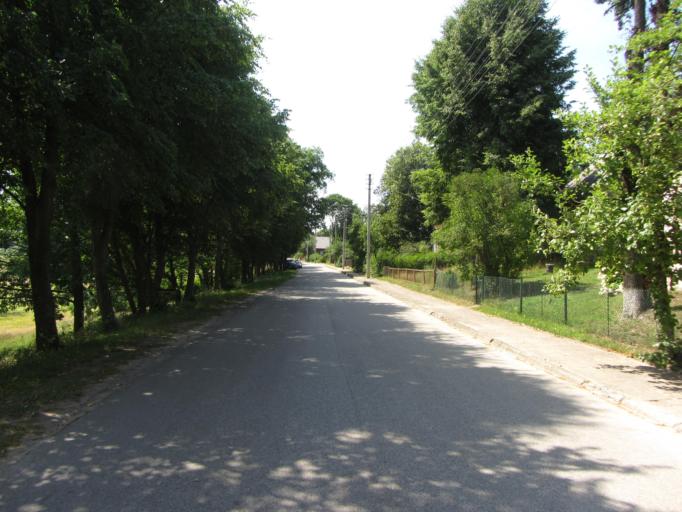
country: LT
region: Alytaus apskritis
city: Druskininkai
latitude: 53.9788
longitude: 23.9450
